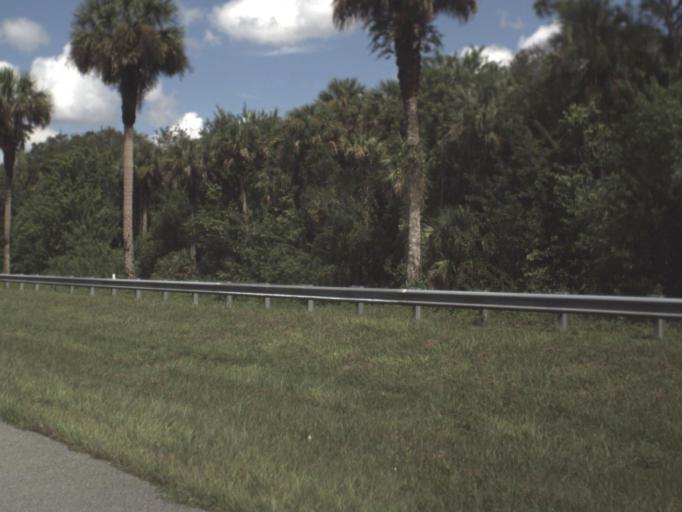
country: US
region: Florida
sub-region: Collier County
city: Immokalee
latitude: 26.2621
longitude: -81.3420
